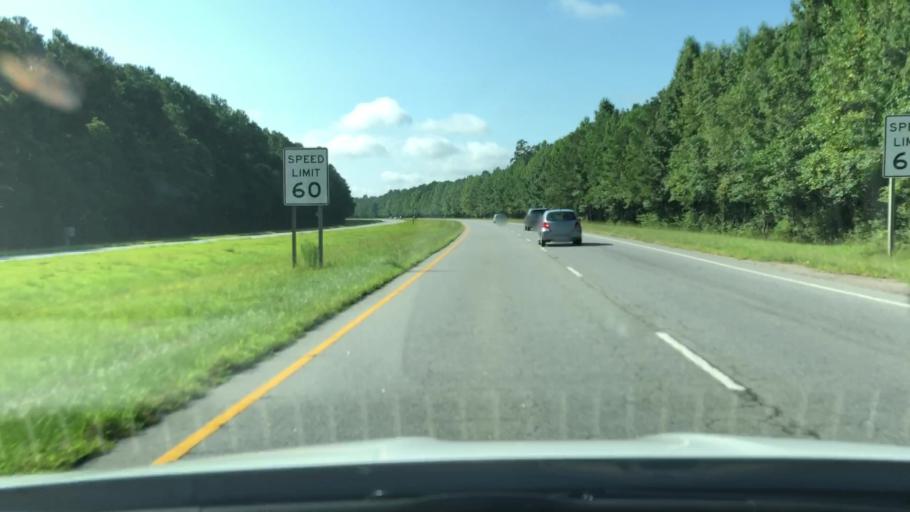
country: US
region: North Carolina
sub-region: Pasquotank County
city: Elizabeth City
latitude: 36.4118
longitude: -76.3403
